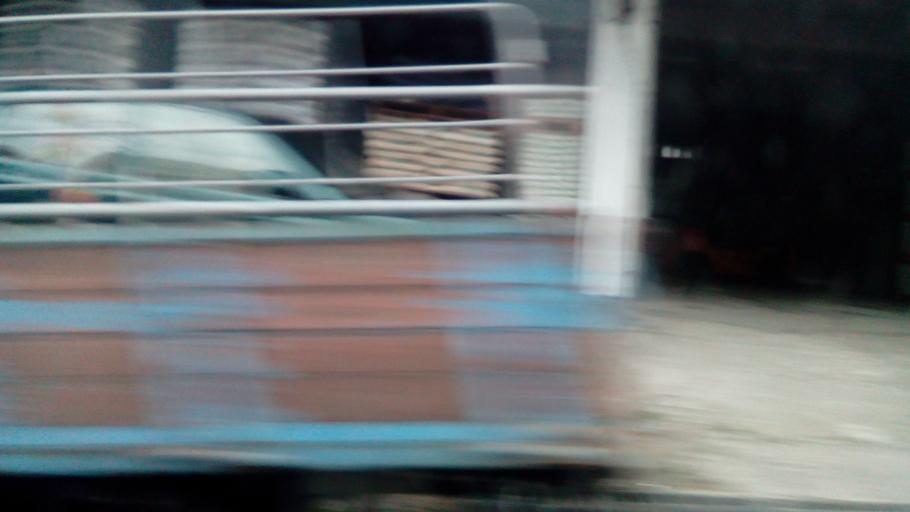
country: TW
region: Taiwan
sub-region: Nantou
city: Puli
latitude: 24.2598
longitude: 121.2561
